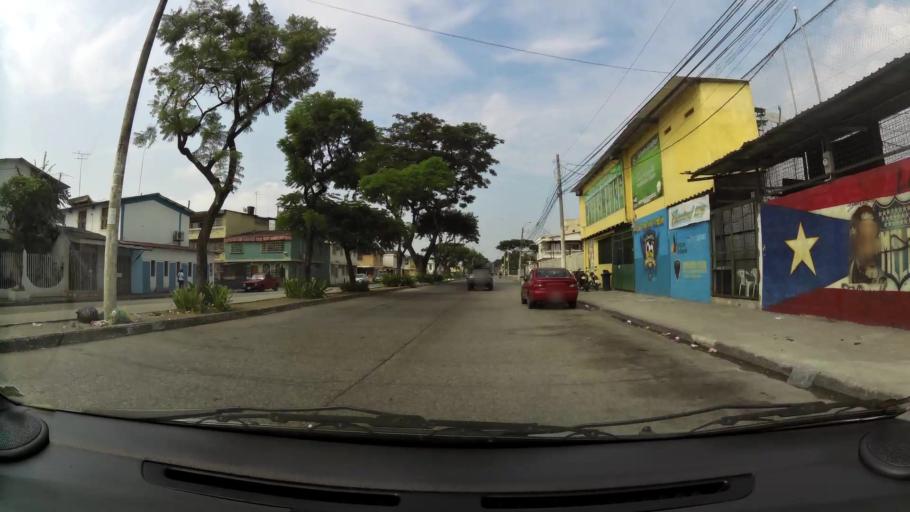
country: EC
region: Guayas
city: Guayaquil
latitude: -2.2449
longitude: -79.9030
